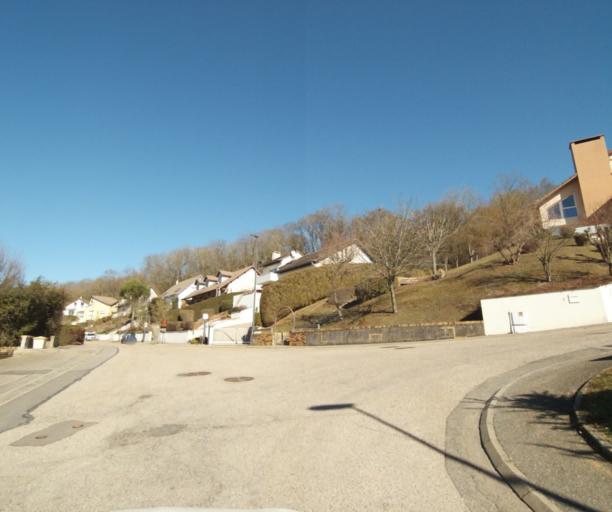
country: FR
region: Lorraine
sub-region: Departement de Meurthe-et-Moselle
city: Essey-les-Nancy
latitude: 48.7154
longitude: 6.2223
